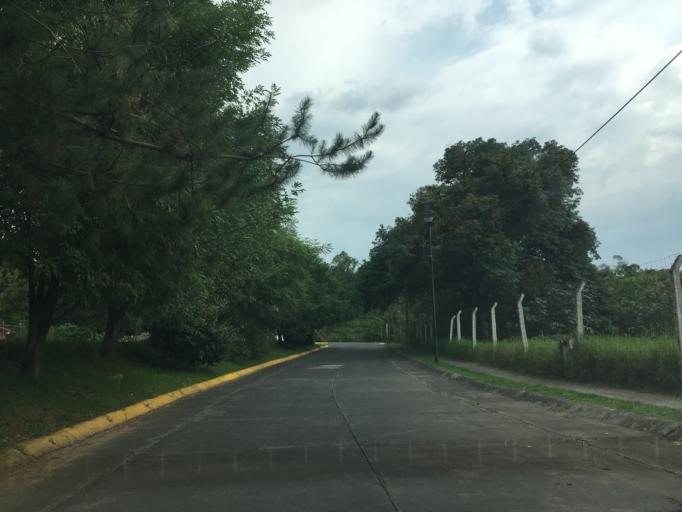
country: MX
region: Michoacan
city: Morelia
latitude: 19.6810
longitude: -101.2062
